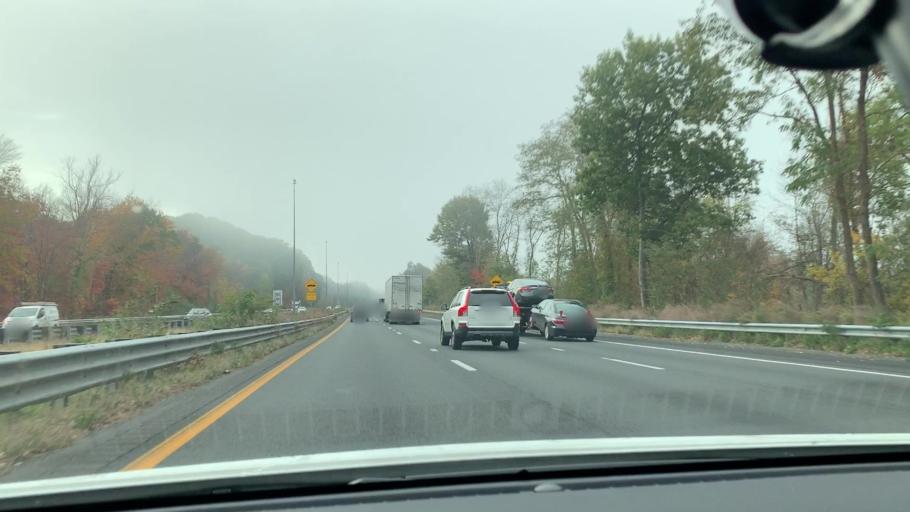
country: US
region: Massachusetts
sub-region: Hampden County
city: Longmeadow
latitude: 42.0431
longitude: -72.5888
